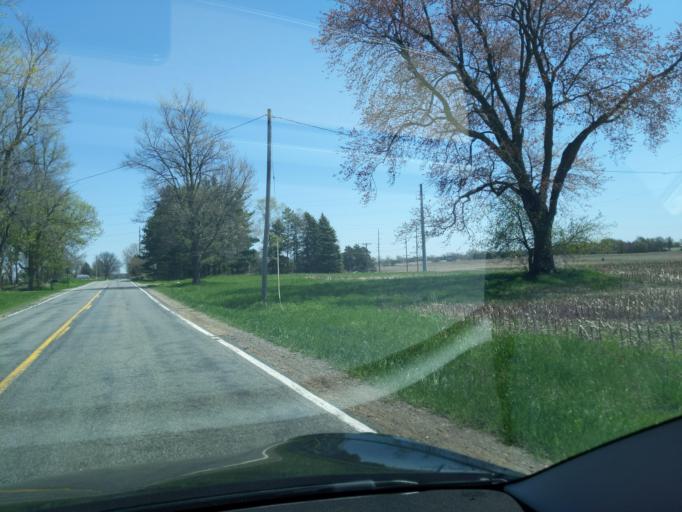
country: US
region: Michigan
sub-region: Ingham County
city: Mason
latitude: 42.5609
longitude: -84.4752
